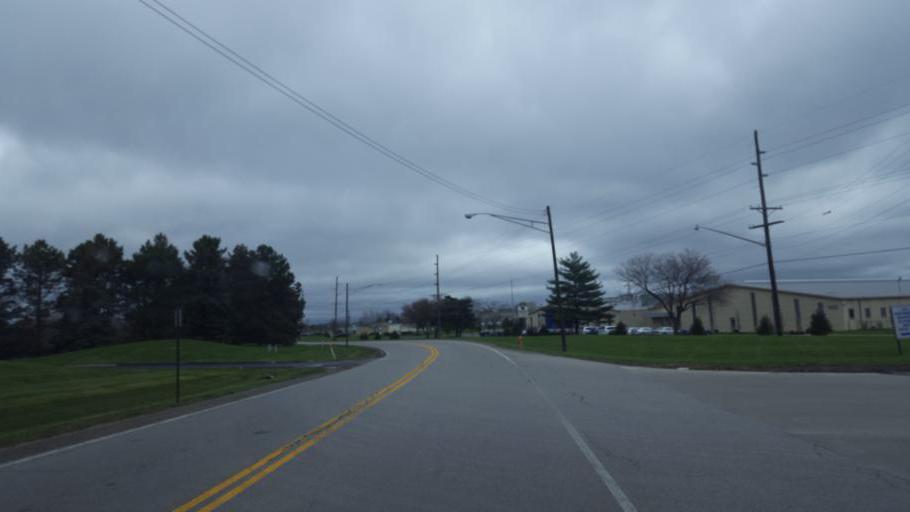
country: US
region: Ohio
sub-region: Franklin County
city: Worthington
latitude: 40.1126
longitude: -82.9948
